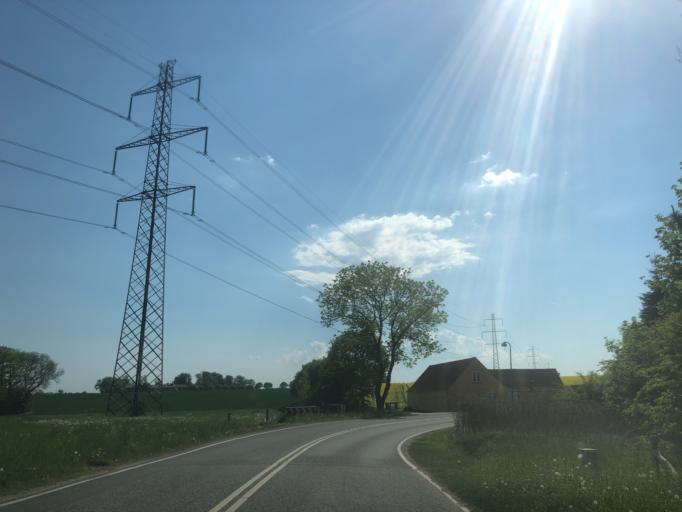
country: DK
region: Capital Region
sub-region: Hoje-Taastrup Kommune
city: Flong
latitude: 55.6284
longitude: 12.2216
